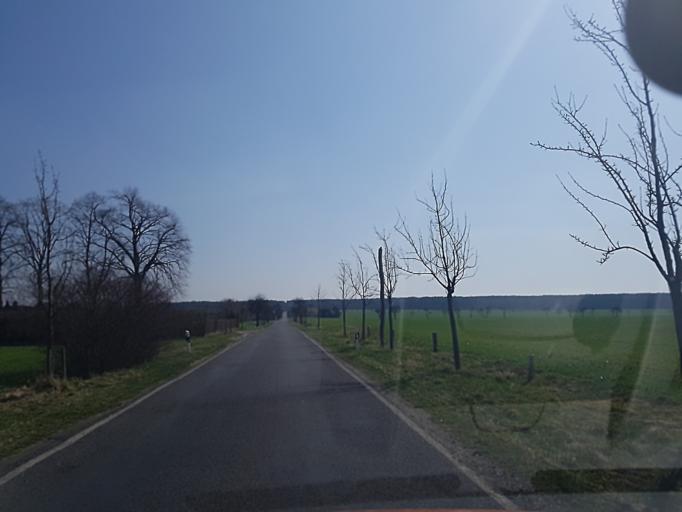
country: DE
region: Saxony
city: Gross Duben
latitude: 51.6673
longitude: 14.5459
